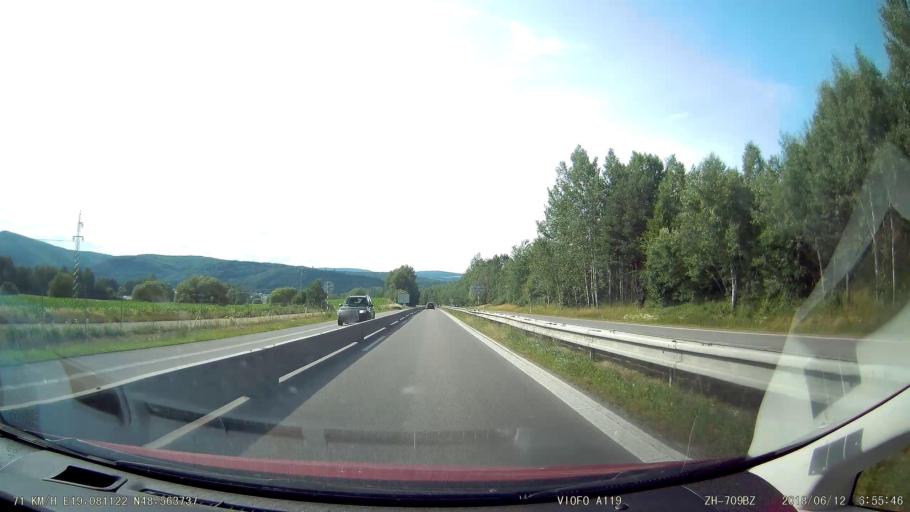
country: SK
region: Banskobystricky
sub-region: Okres Banska Bystrica
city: Zvolen
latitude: 48.5641
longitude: 19.0810
